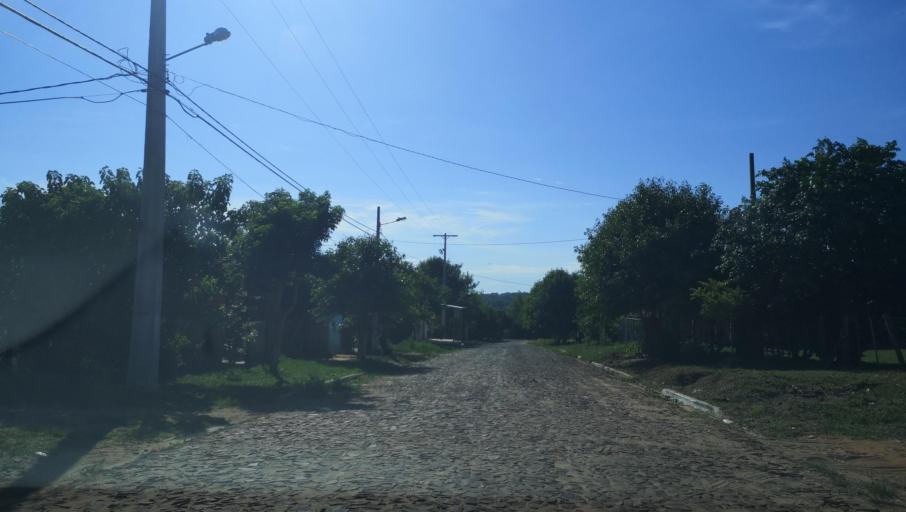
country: PY
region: Misiones
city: Santa Maria
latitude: -26.8771
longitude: -57.0076
